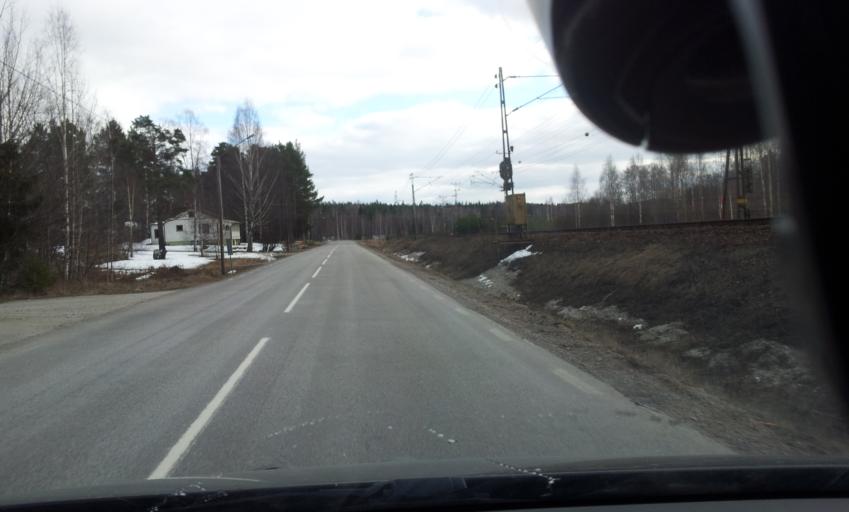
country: SE
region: Vaesternorrland
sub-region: Ange Kommun
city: Ange
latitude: 62.1684
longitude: 15.6754
